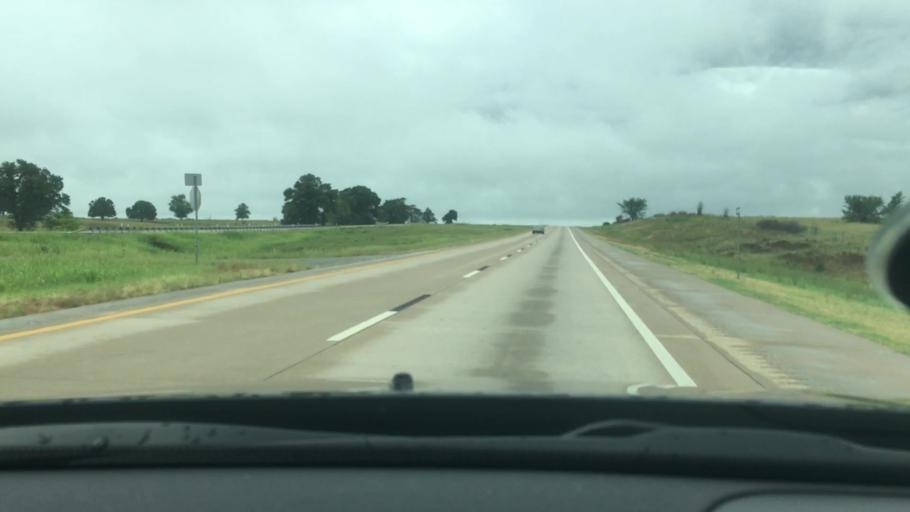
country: US
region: Oklahoma
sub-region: Atoka County
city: Atoka
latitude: 34.2281
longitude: -96.2253
